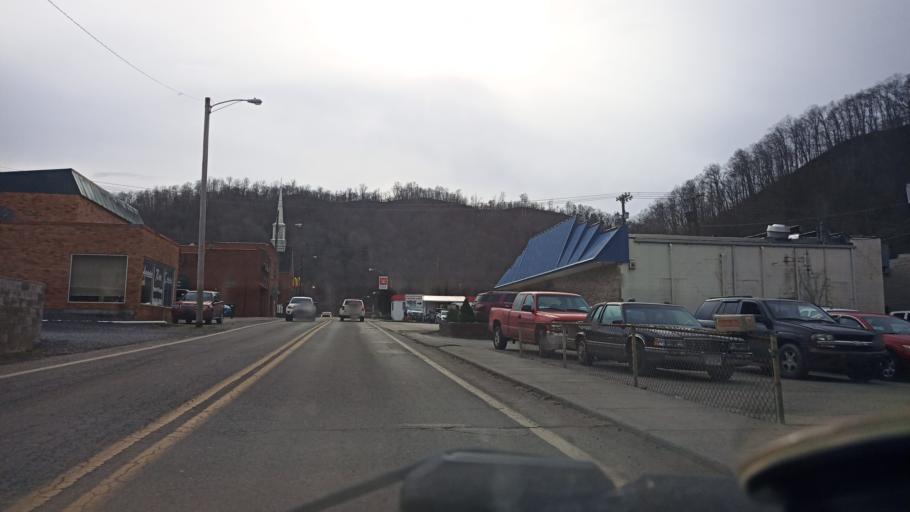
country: US
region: West Virginia
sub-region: Mingo County
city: Gilbert Creek
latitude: 37.6160
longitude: -81.8657
